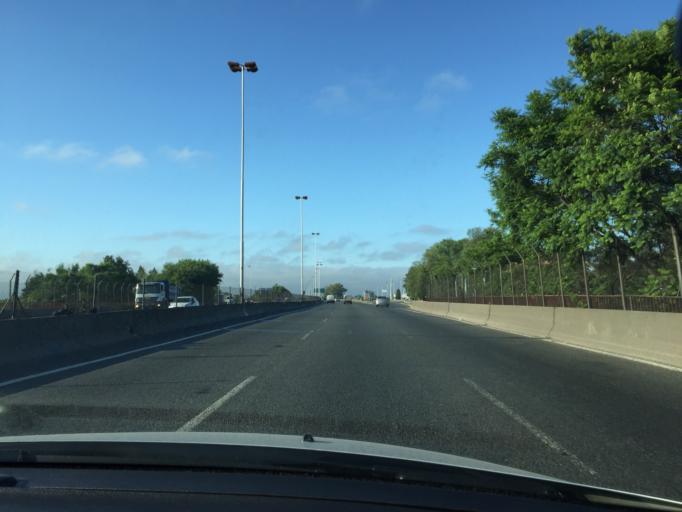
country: AR
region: Buenos Aires F.D.
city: Villa Lugano
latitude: -34.7228
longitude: -58.5137
